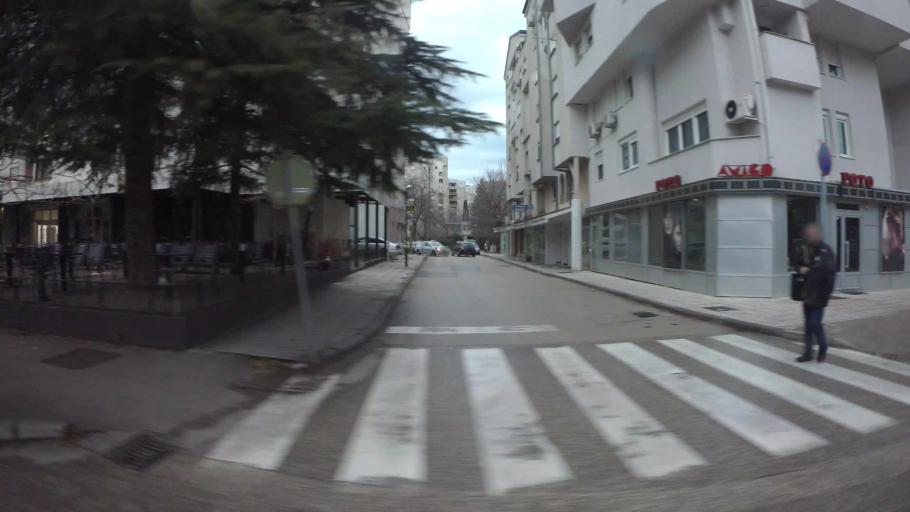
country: BA
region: Federation of Bosnia and Herzegovina
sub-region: Hercegovacko-Bosanski Kanton
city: Mostar
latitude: 43.3460
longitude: 17.8025
